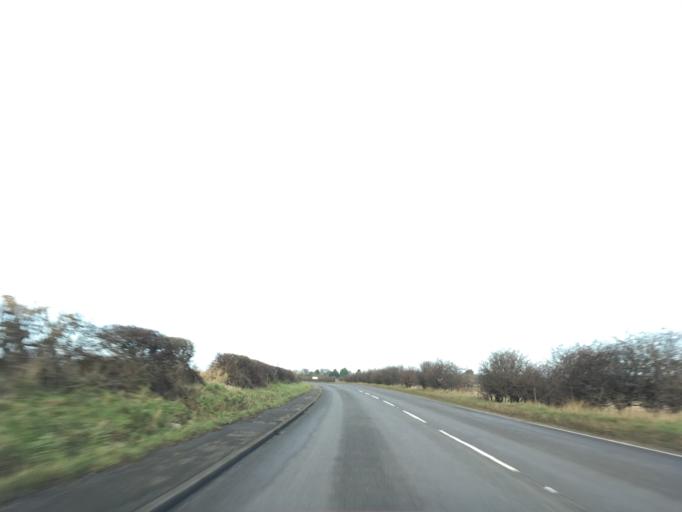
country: GB
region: England
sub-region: Nottinghamshire
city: South Collingham
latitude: 53.1673
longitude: -0.7652
